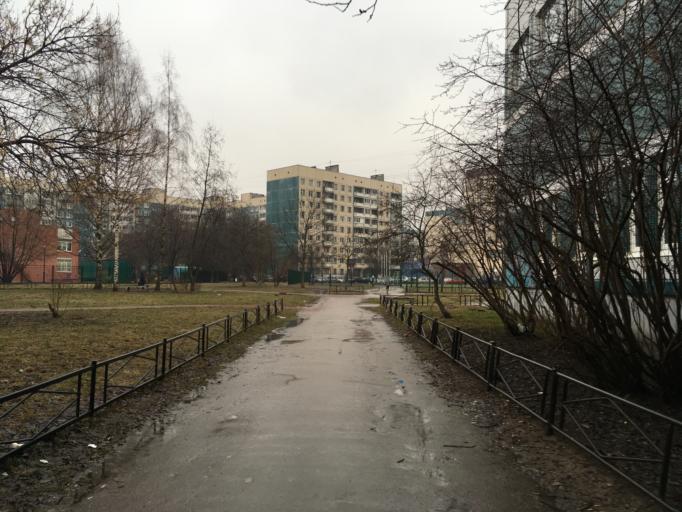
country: RU
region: St.-Petersburg
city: Komendantsky aerodrom
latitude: 60.0130
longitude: 30.2594
